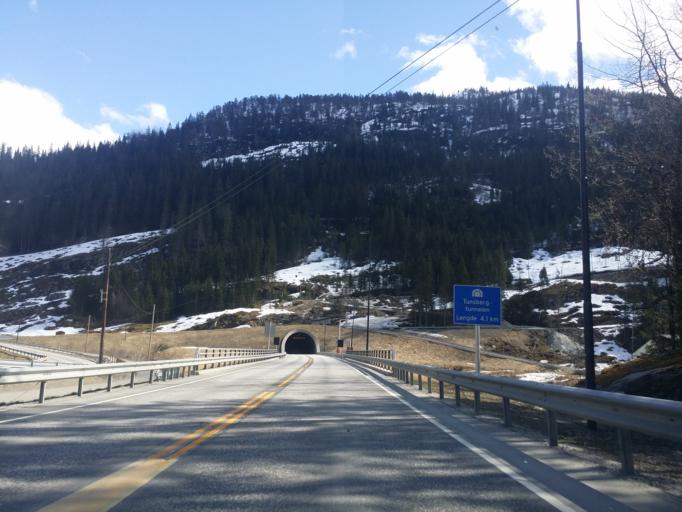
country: NO
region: Hordaland
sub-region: Granvin
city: Granvin
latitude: 60.5858
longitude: 6.6113
